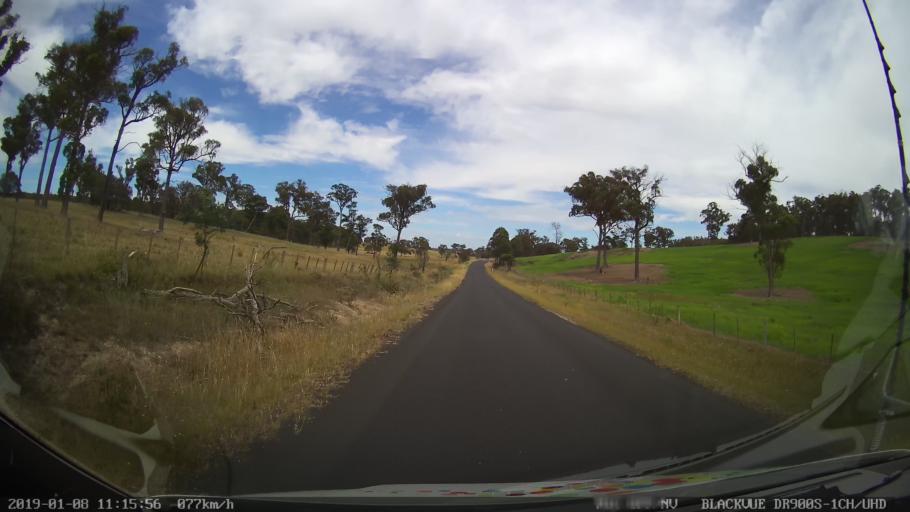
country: AU
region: New South Wales
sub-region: Guyra
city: Guyra
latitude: -30.2219
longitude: 151.5707
